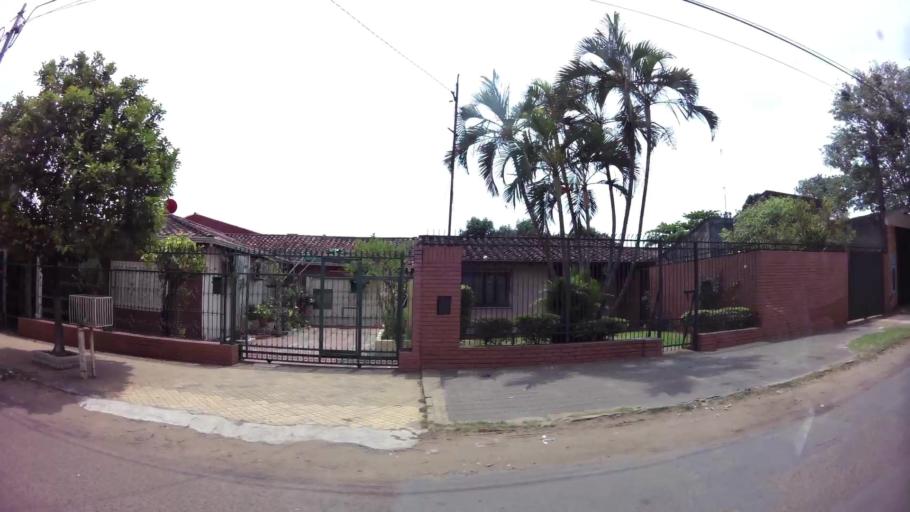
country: PY
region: Central
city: Fernando de la Mora
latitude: -25.3171
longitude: -57.5621
